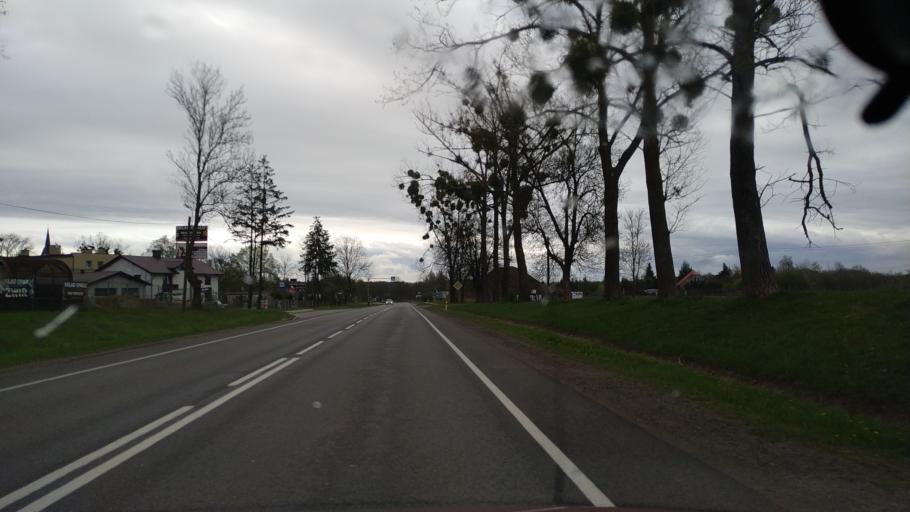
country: PL
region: Pomeranian Voivodeship
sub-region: Powiat starogardzki
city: Zblewo
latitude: 53.9296
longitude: 18.3199
